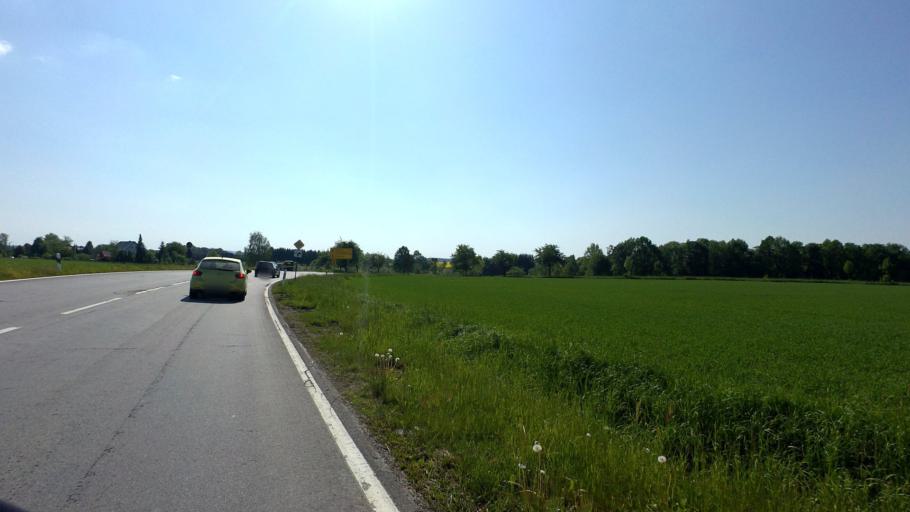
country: DE
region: Saxony
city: Hohnstein
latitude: 51.0073
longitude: 14.0847
